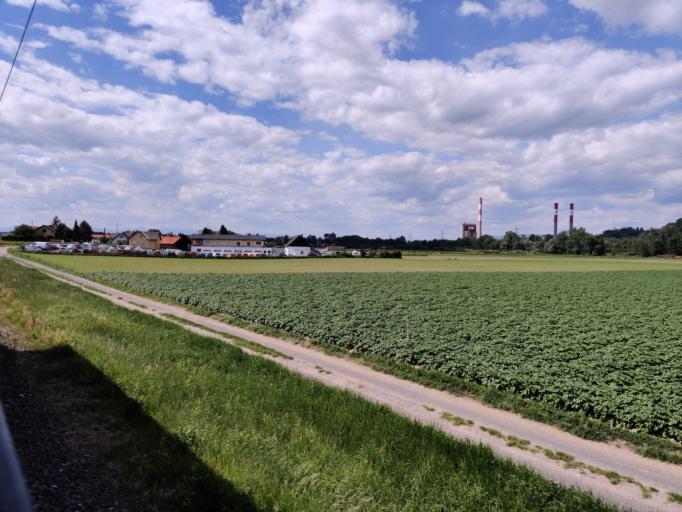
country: AT
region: Styria
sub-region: Politischer Bezirk Leibnitz
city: Weitendorf
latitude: 46.8952
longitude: 15.4924
